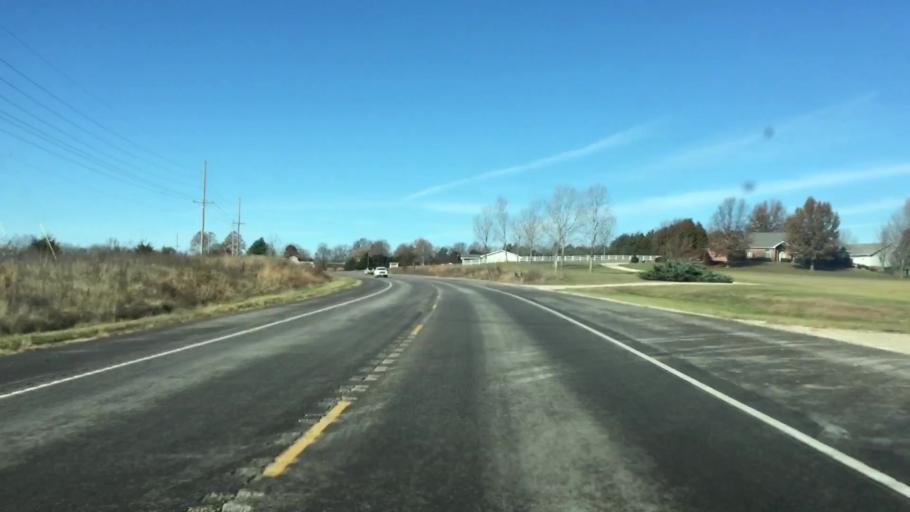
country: US
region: Missouri
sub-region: Miller County
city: Eldon
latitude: 38.3726
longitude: -92.6201
